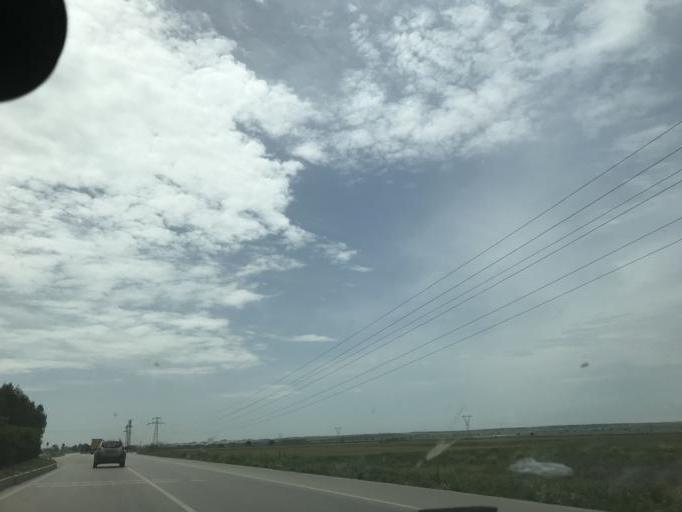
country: TR
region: Adana
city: Ceyhan
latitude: 37.0252
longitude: 35.7299
